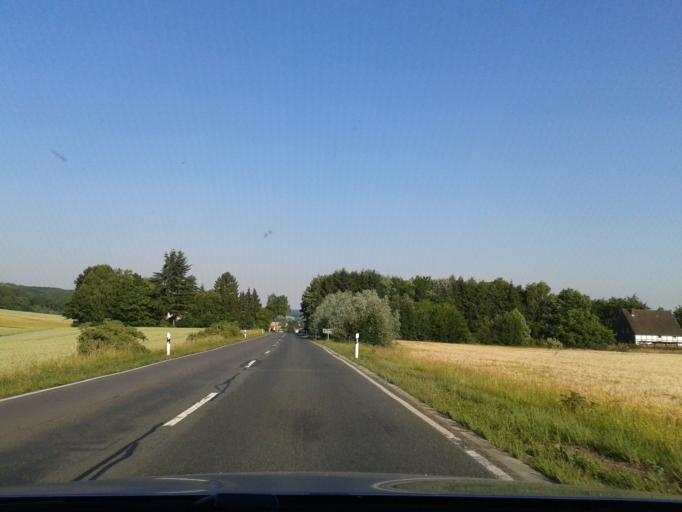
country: DE
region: North Rhine-Westphalia
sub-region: Regierungsbezirk Detmold
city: Barntrup
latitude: 51.9749
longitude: 9.1778
